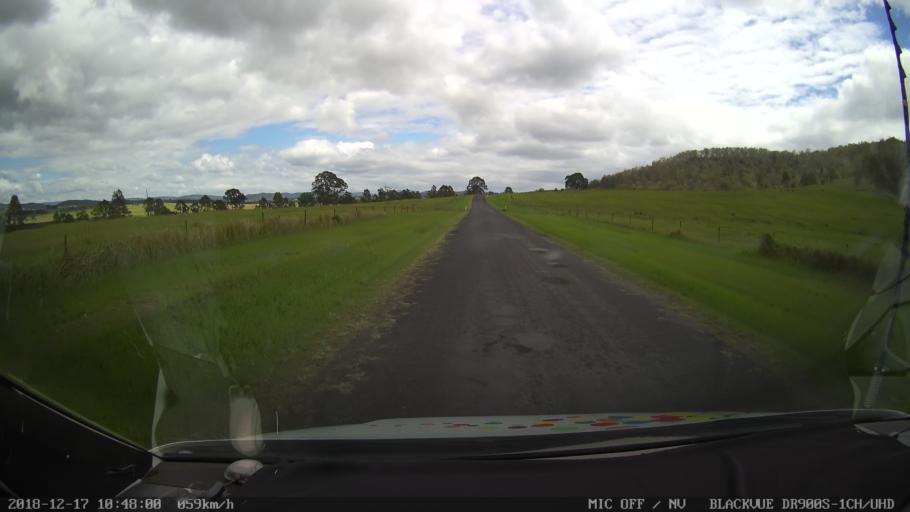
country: AU
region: New South Wales
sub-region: Clarence Valley
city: Gordon
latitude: -28.8766
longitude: 152.5706
